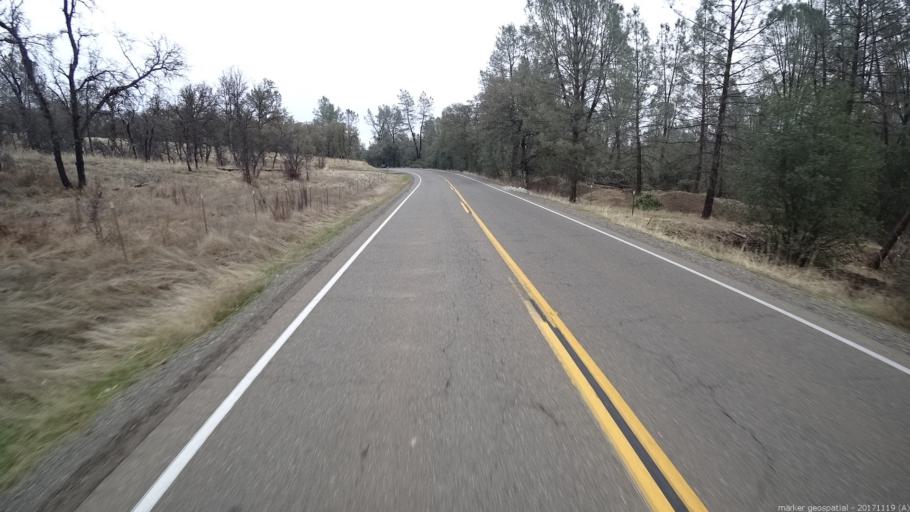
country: US
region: California
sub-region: Shasta County
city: Redding
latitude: 40.4942
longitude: -122.3872
